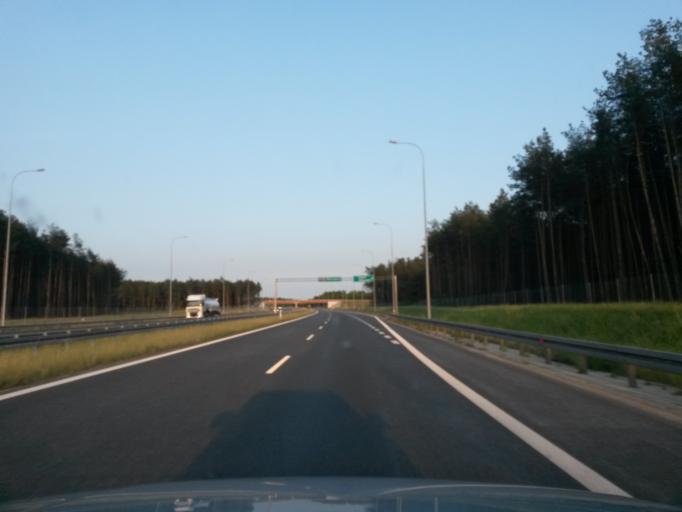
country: PL
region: Lodz Voivodeship
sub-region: Powiat wieruszowski
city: Wieruszow
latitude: 51.3098
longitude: 18.1796
